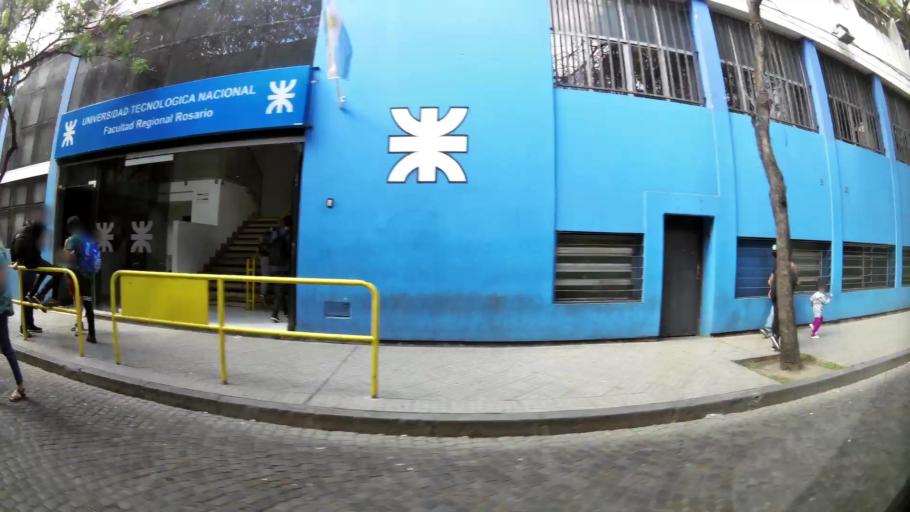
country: AR
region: Santa Fe
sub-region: Departamento de Rosario
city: Rosario
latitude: -32.9544
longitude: -60.6438
